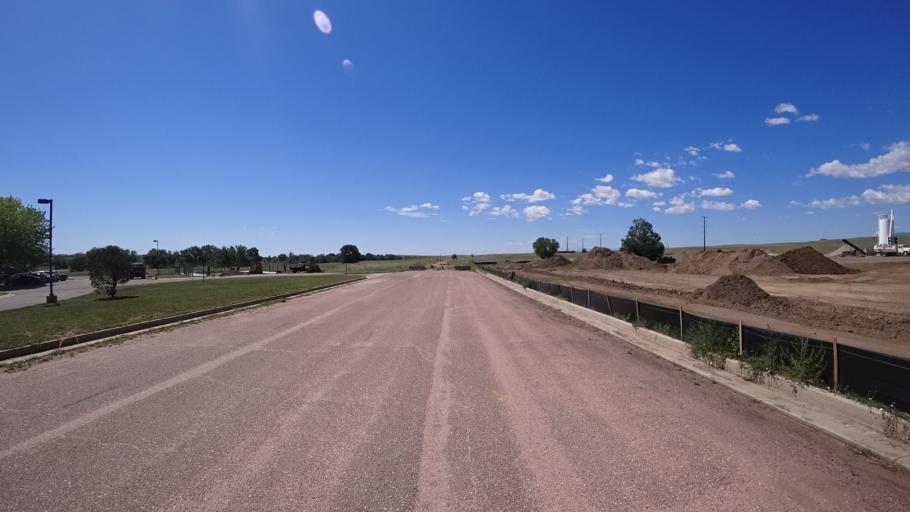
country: US
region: Colorado
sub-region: El Paso County
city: Security-Widefield
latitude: 38.7801
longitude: -104.6620
